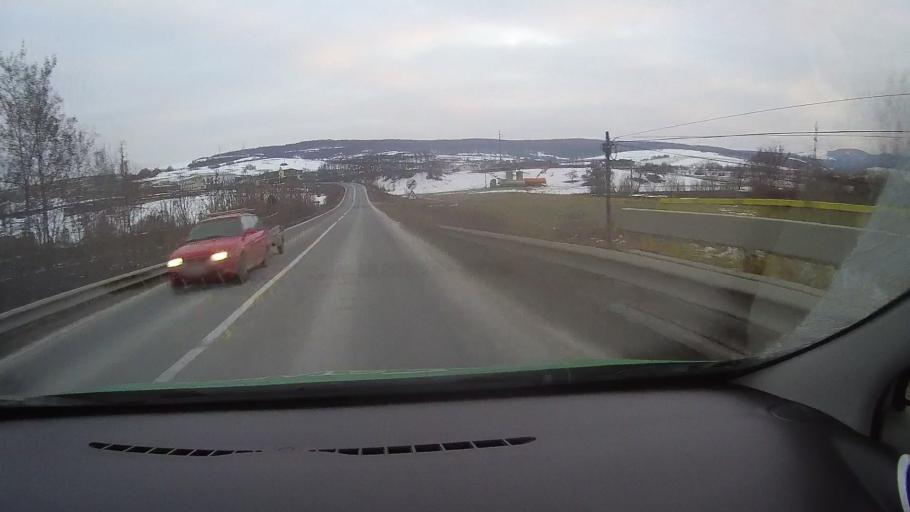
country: RO
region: Harghita
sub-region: Comuna Lupeni
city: Lupeni
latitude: 46.3582
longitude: 25.2387
